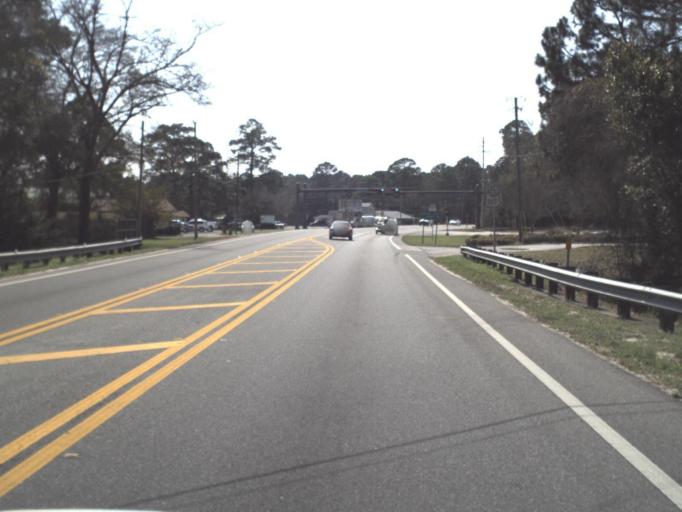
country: US
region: Florida
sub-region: Bay County
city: Pretty Bayou
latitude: 30.1997
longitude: -85.6825
